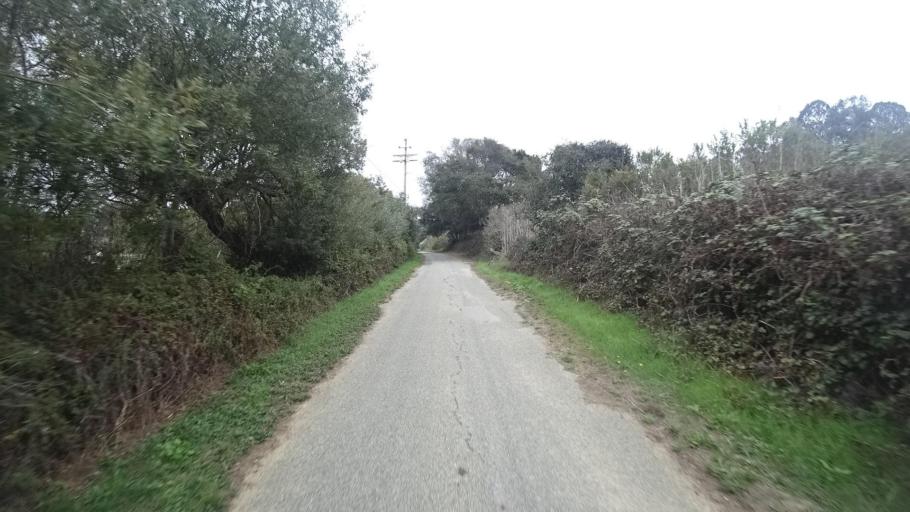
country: US
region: California
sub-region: Monterey County
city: Las Lomas
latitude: 36.8667
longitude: -121.7613
